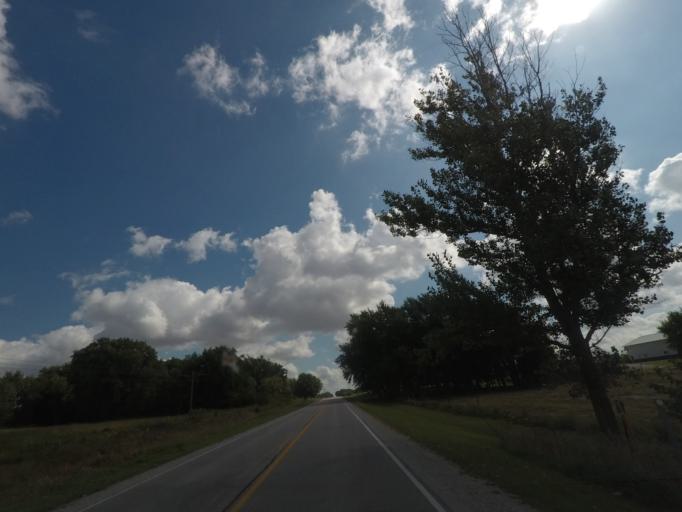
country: US
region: Iowa
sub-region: Story County
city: Nevada
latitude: 42.0225
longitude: -93.3355
